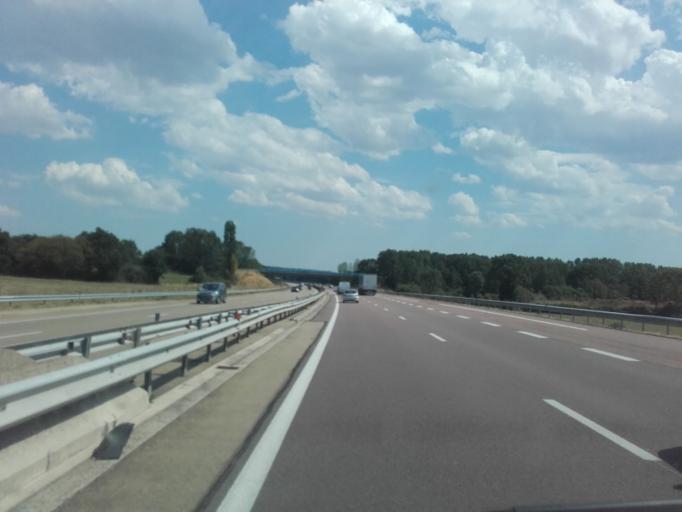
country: FR
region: Bourgogne
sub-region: Departement de l'Yonne
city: Avallon
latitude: 47.5115
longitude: 3.9975
